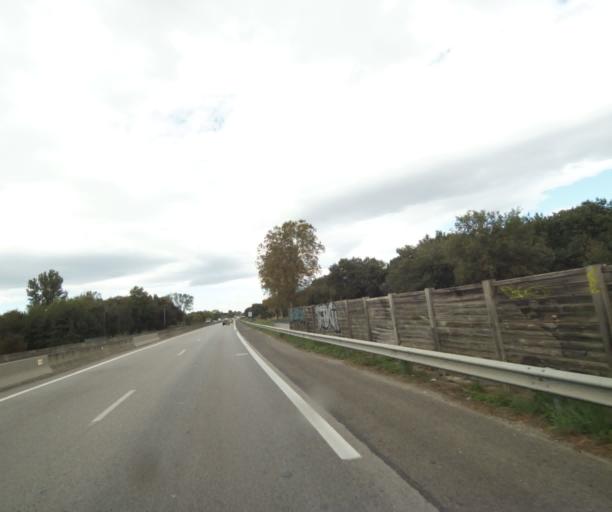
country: FR
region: Languedoc-Roussillon
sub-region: Departement des Pyrenees-Orientales
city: Argelers
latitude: 42.5687
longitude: 3.0008
